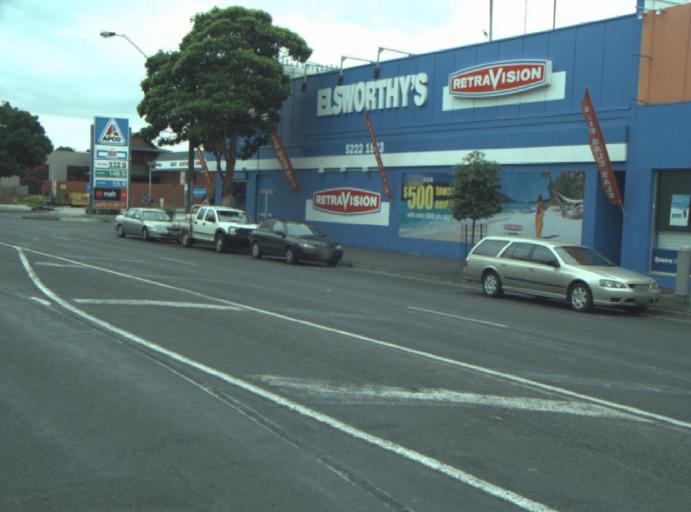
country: AU
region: Victoria
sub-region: Greater Geelong
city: Geelong
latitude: -38.1591
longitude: 144.3553
